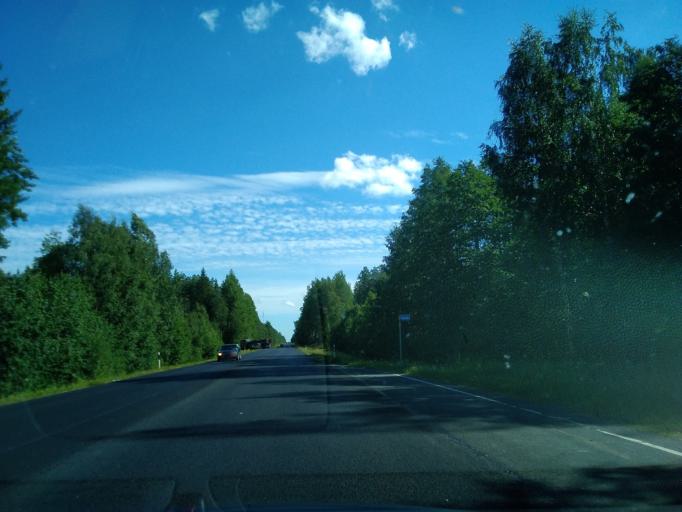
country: FI
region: Haeme
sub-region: Haemeenlinna
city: Renko
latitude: 60.9291
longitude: 24.3538
